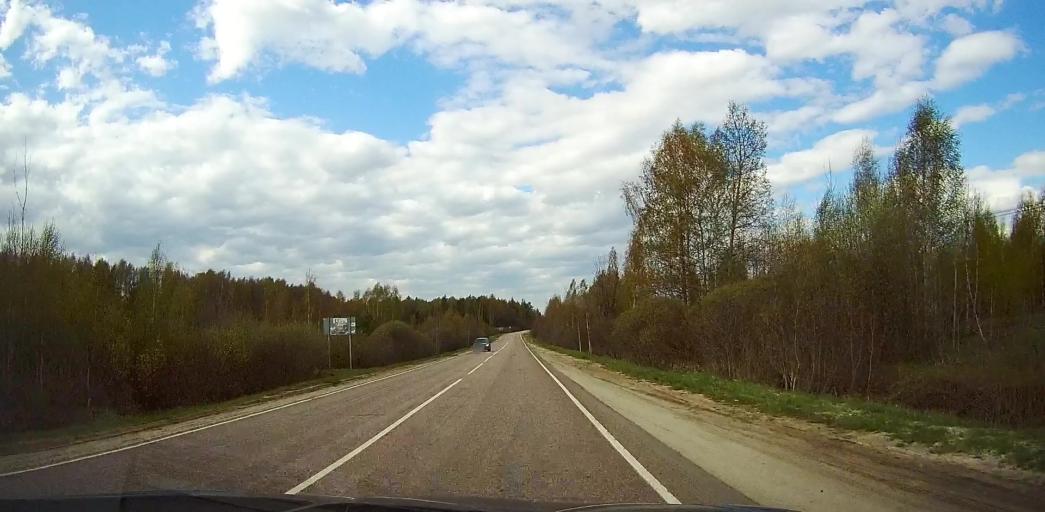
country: RU
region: Moskovskaya
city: Rakhmanovo
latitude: 55.6782
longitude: 38.6442
